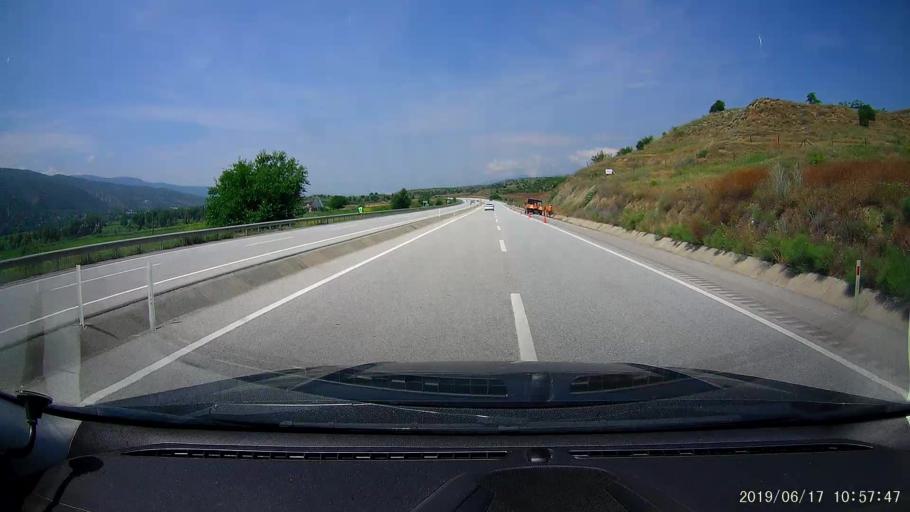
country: TR
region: Kastamonu
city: Tosya
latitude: 41.0477
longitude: 34.2397
